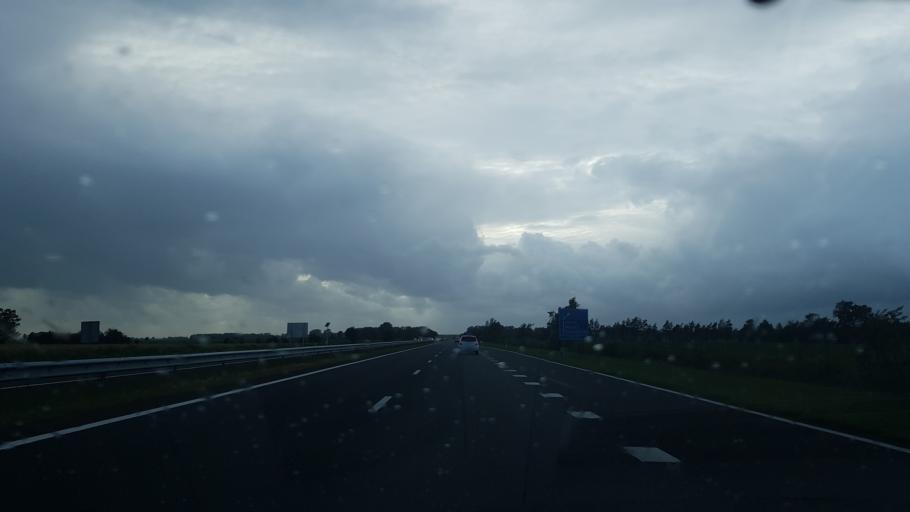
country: NL
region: Friesland
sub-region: Gemeente Tytsjerksteradiel
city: Garyp
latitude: 53.1562
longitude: 5.9650
